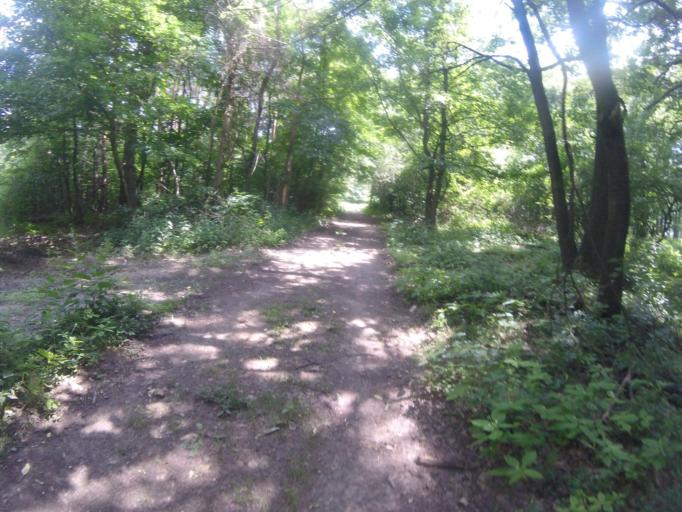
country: HU
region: Fejer
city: Szarliget
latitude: 47.5036
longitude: 18.4335
